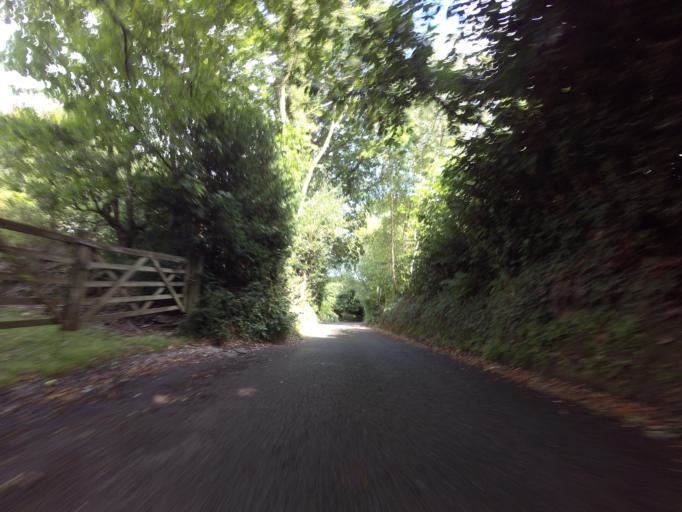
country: GB
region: England
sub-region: Kent
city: Borough Green
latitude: 51.2860
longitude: 0.2769
